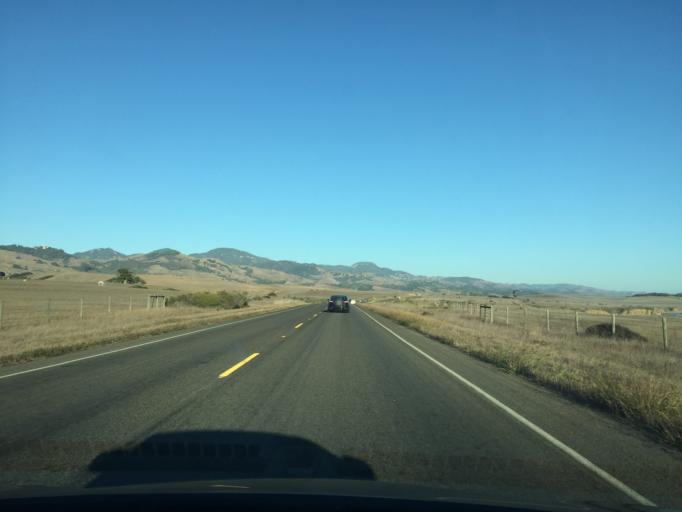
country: US
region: California
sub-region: San Luis Obispo County
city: Cambria
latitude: 35.6528
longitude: -121.2259
